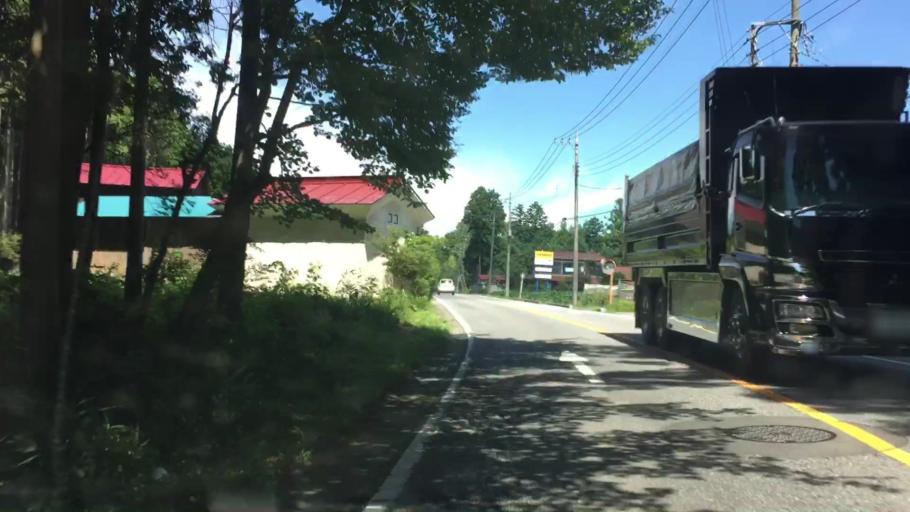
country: JP
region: Tochigi
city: Imaichi
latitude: 36.7146
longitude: 139.7521
